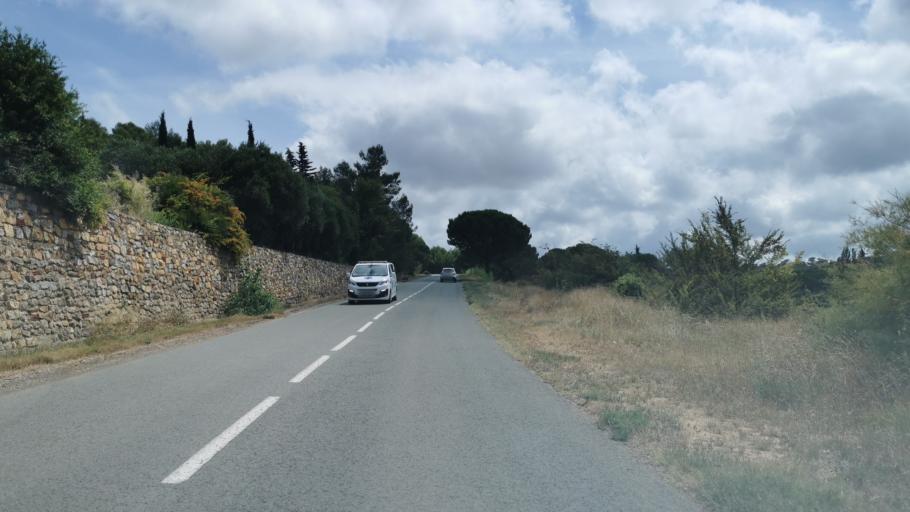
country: FR
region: Languedoc-Roussillon
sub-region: Departement de l'Aude
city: Bizanet
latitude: 43.1653
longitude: 2.8845
